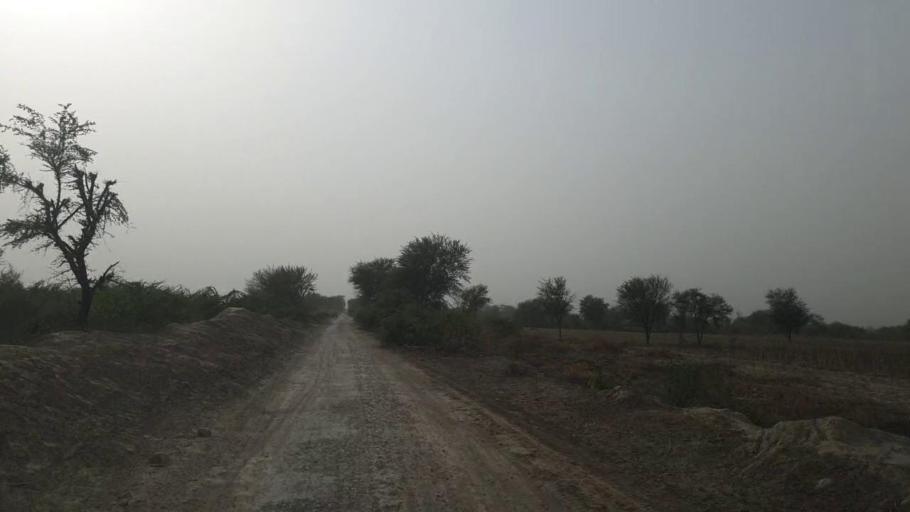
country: PK
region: Sindh
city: Kunri
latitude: 25.0678
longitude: 69.4895
